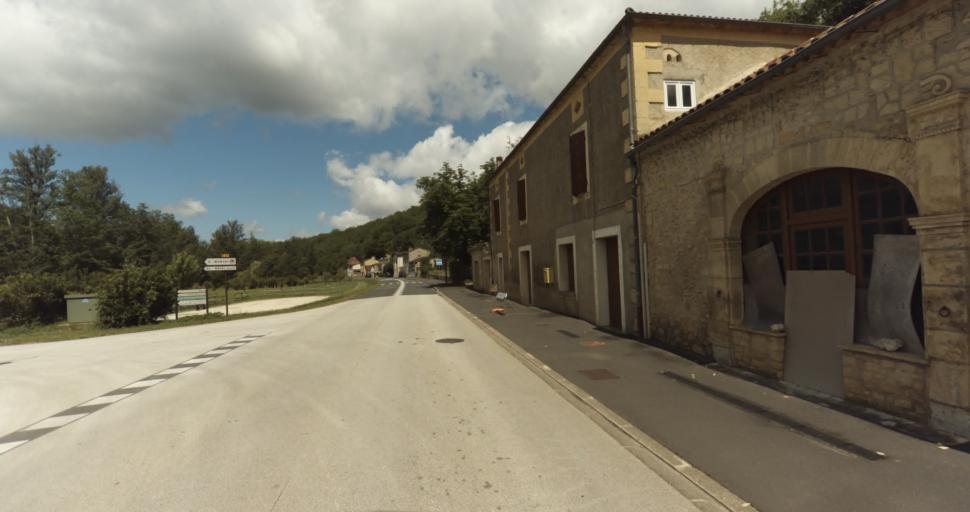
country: FR
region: Aquitaine
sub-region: Departement de la Dordogne
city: Lalinde
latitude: 44.8046
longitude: 0.7309
